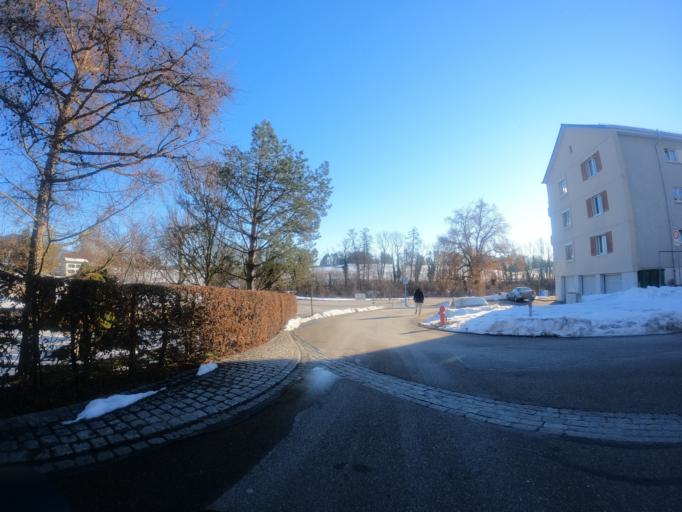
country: CH
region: Zurich
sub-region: Bezirk Affoltern
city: Affoltern / Unterdorf
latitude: 47.2874
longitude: 8.4394
